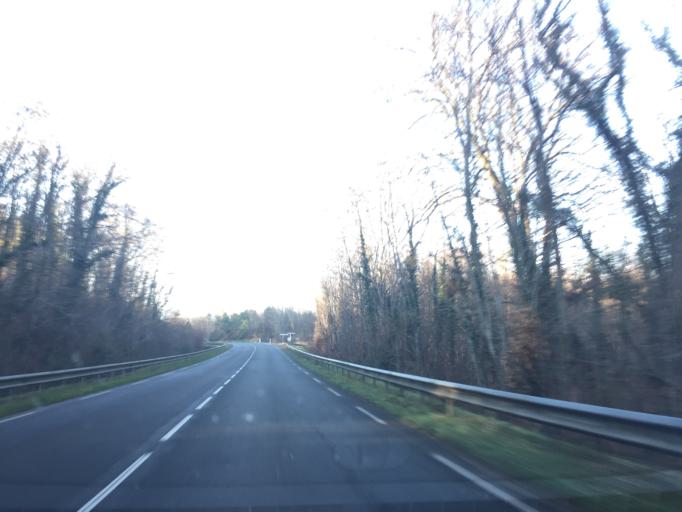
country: FR
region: Aquitaine
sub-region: Departement de la Dordogne
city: Riberac
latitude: 45.1840
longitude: 0.3822
